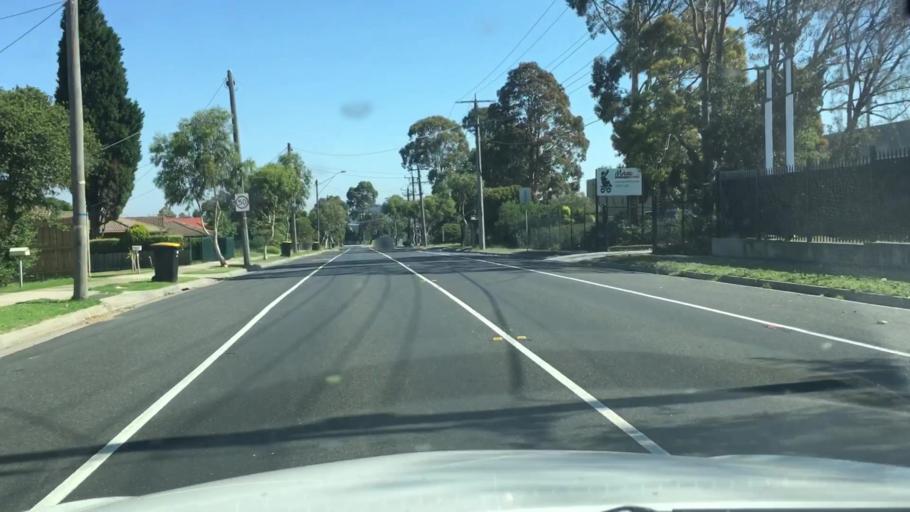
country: AU
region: Victoria
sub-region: Greater Dandenong
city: Noble Park North
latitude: -37.9470
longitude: 145.1877
